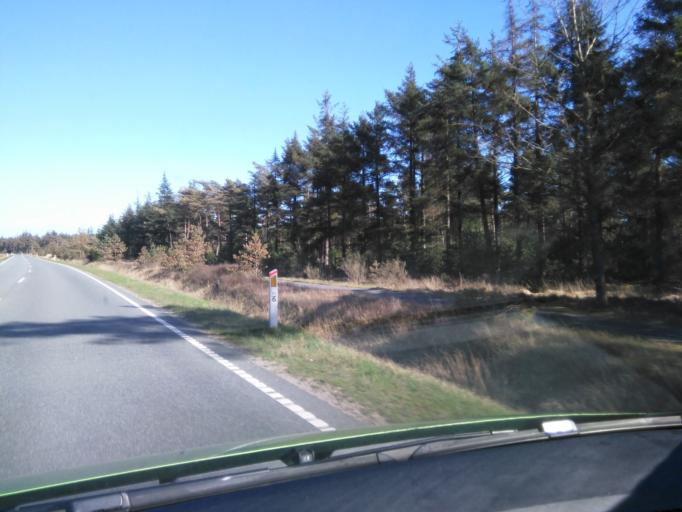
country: DK
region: South Denmark
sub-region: Varde Kommune
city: Oksbol
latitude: 55.5686
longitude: 8.1930
